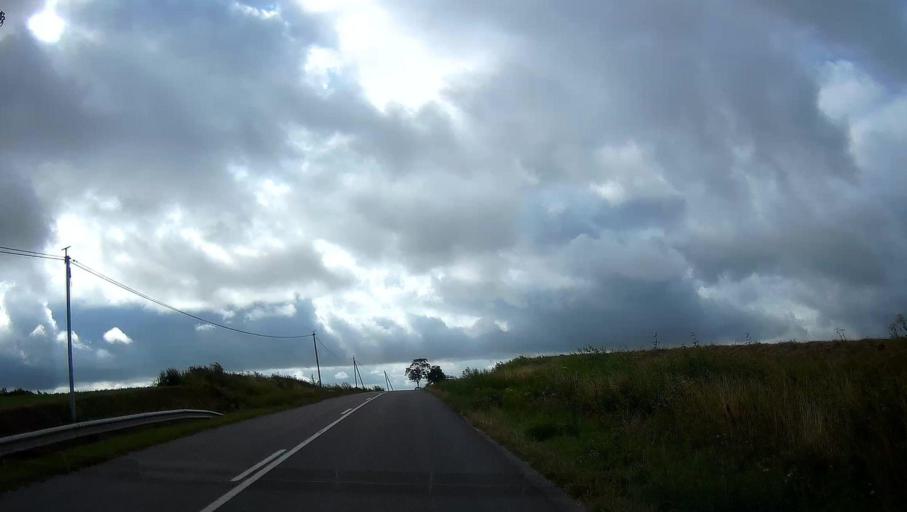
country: FR
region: Champagne-Ardenne
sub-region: Departement des Ardennes
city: Chateau-Porcien
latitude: 49.5943
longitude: 4.2397
